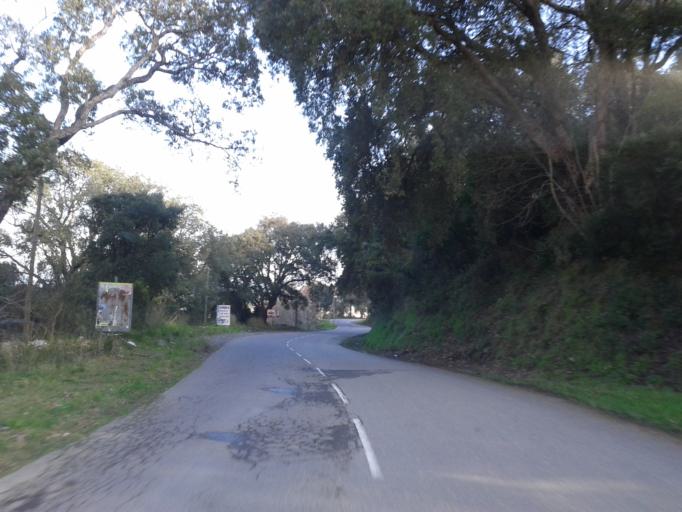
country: FR
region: Corsica
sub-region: Departement de la Haute-Corse
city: Biguglia
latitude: 42.5959
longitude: 9.4236
